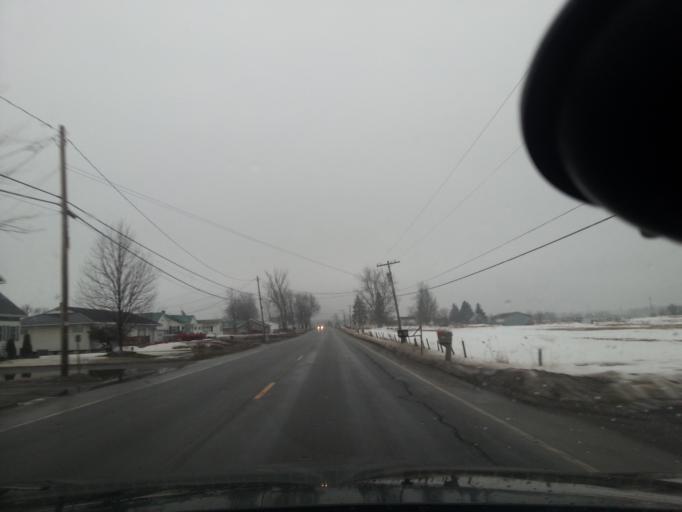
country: US
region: New York
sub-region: St. Lawrence County
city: Ogdensburg
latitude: 44.6699
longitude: -75.4711
